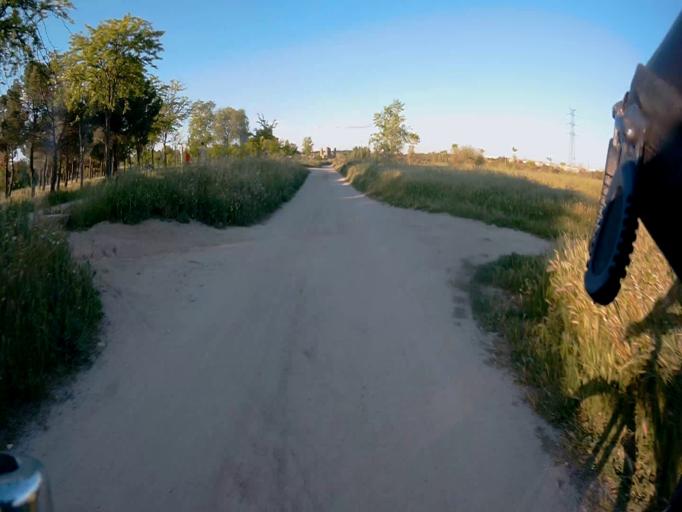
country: ES
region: Madrid
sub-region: Provincia de Madrid
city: Fuenlabrada
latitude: 40.3155
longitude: -3.7990
